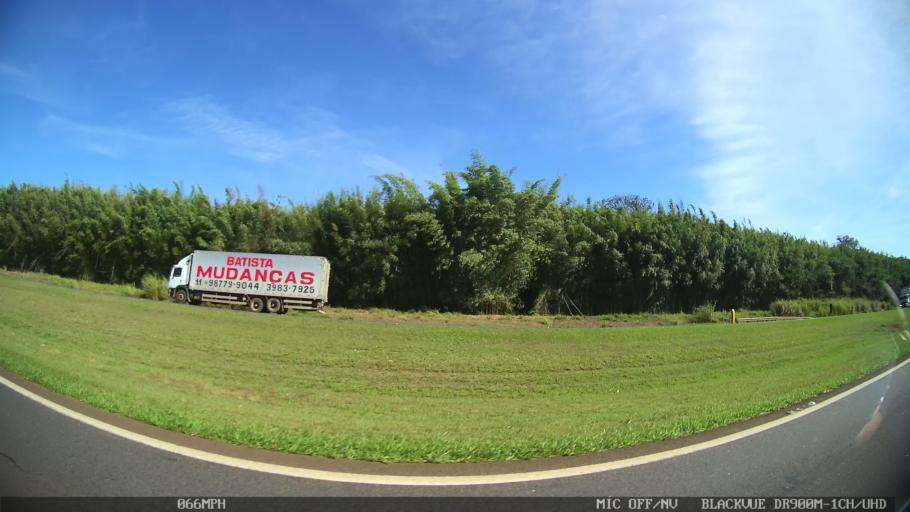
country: BR
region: Sao Paulo
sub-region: Araras
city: Araras
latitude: -22.2815
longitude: -47.3930
